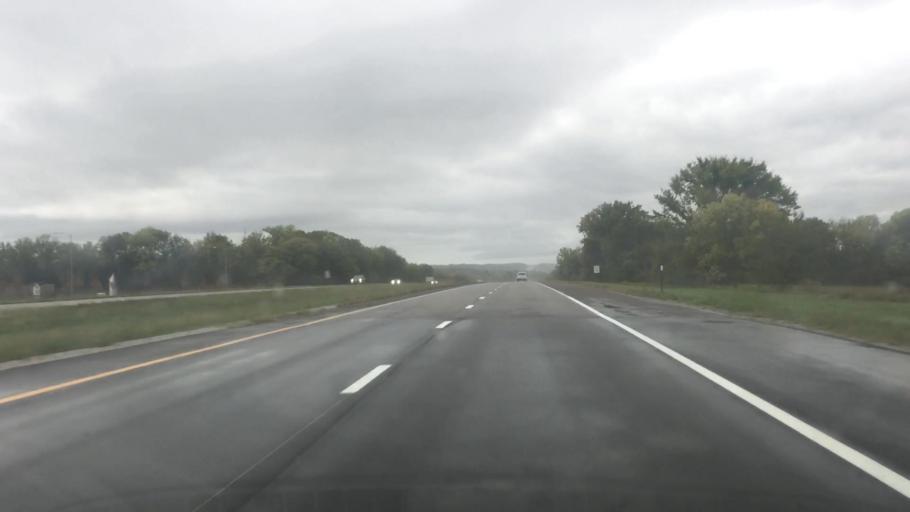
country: US
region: Kansas
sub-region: Johnson County
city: Spring Hill
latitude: 38.7190
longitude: -94.8347
